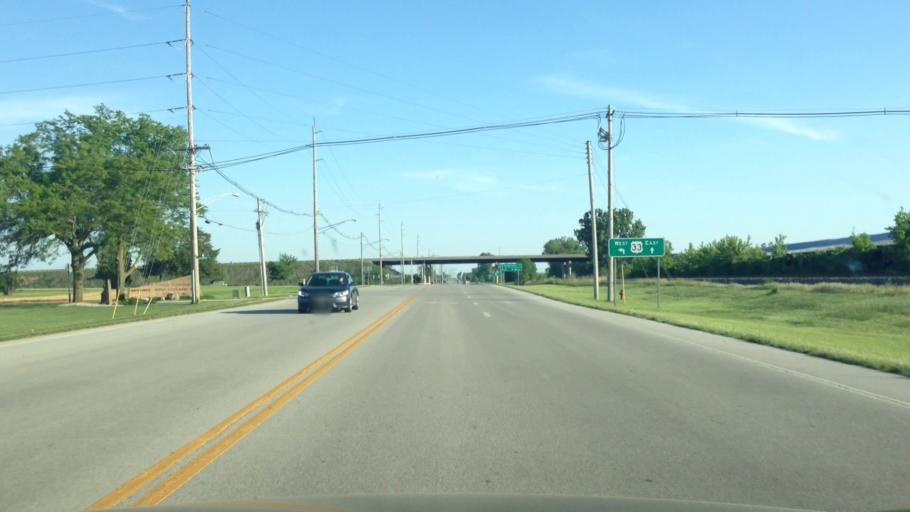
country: US
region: Ohio
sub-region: Auglaize County
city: Wapakoneta
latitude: 40.5589
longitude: -84.1940
